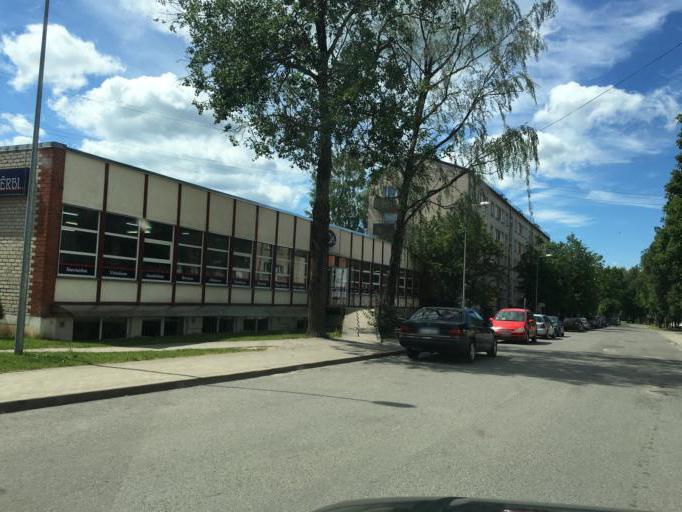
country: LV
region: Balvu Rajons
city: Balvi
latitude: 57.1303
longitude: 27.2671
